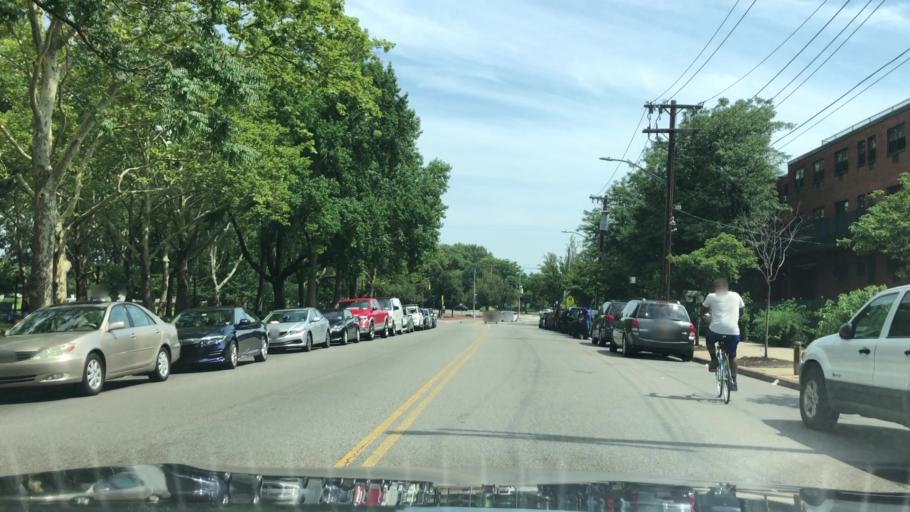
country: US
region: New York
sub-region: Queens County
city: Jamaica
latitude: 40.6742
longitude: -73.7891
